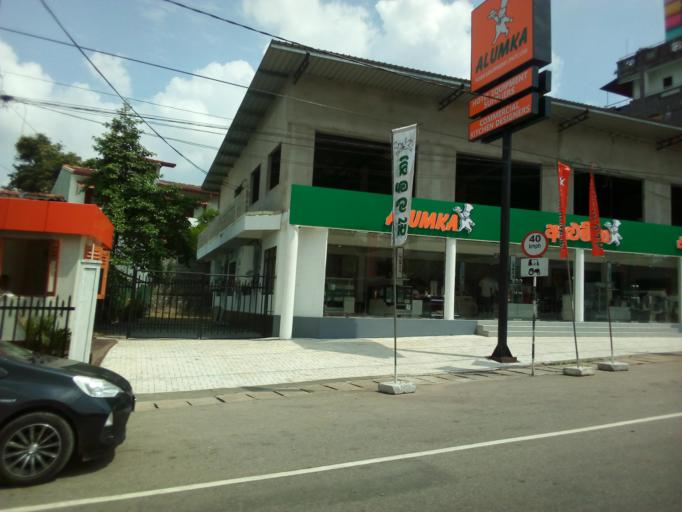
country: LK
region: Western
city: Homagama
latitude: 6.8391
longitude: 79.9719
